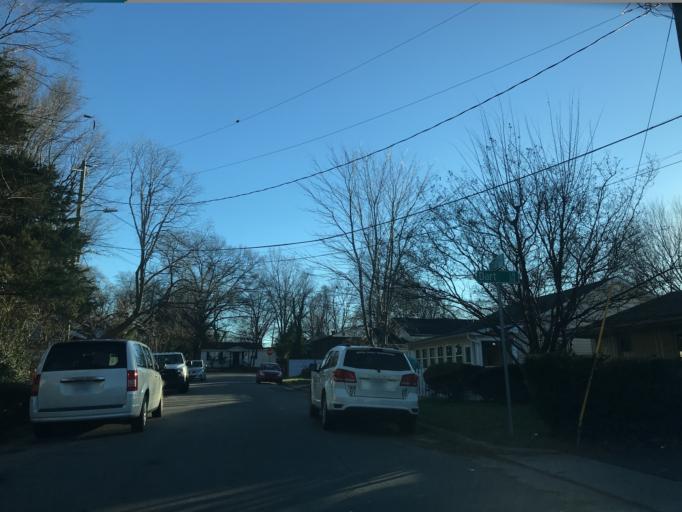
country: US
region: North Carolina
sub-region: Wake County
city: Raleigh
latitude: 35.7828
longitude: -78.6234
